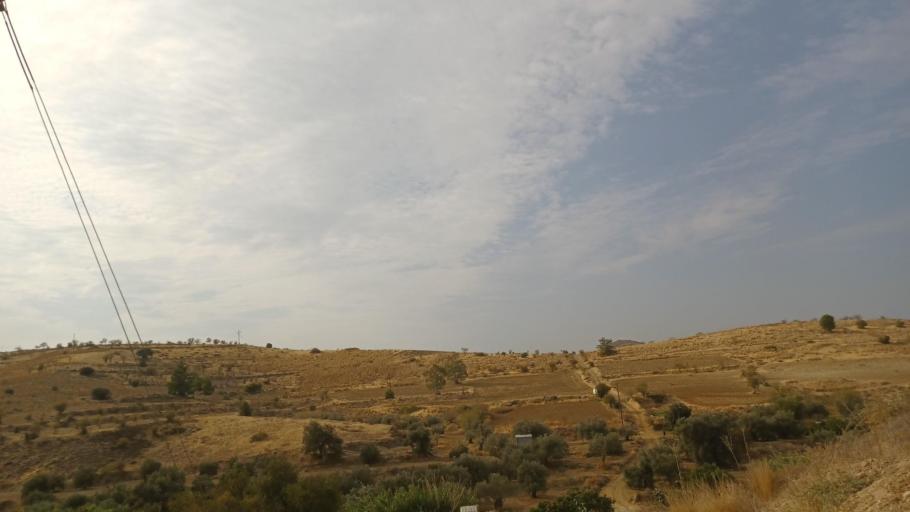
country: CY
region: Lefkosia
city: Peristerona
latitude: 35.0616
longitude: 33.0888
